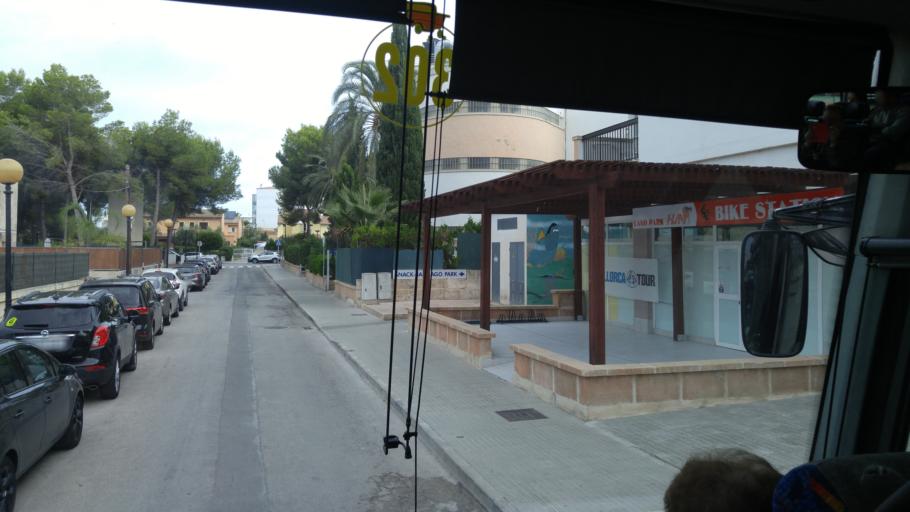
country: ES
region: Balearic Islands
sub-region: Illes Balears
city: Port d'Alcudia
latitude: 39.8142
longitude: 3.1135
